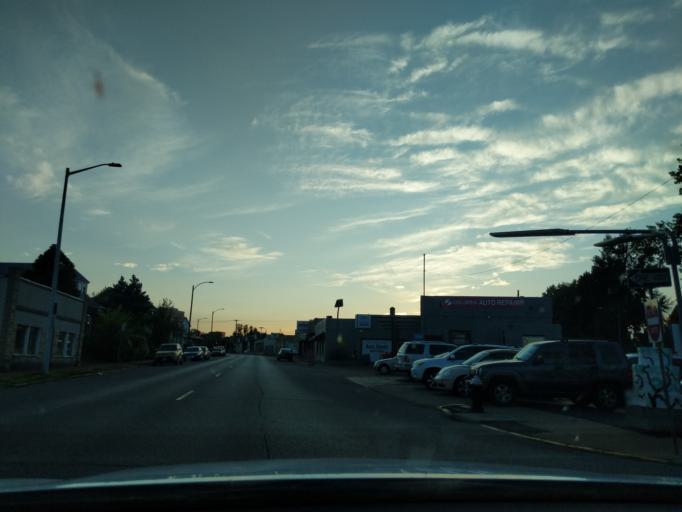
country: US
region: Missouri
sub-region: Saint Louis County
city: Richmond Heights
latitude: 38.6109
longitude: -90.2760
